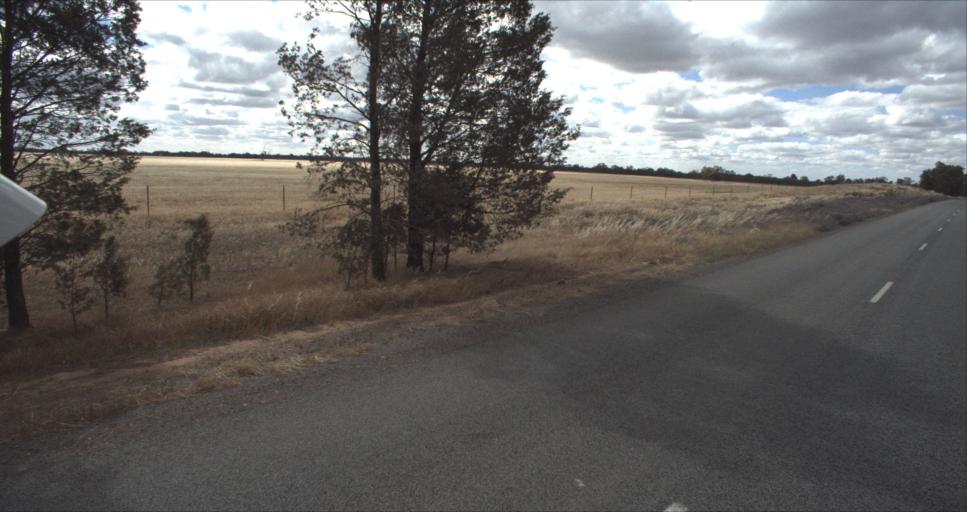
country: AU
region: New South Wales
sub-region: Leeton
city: Leeton
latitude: -34.6752
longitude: 146.3467
